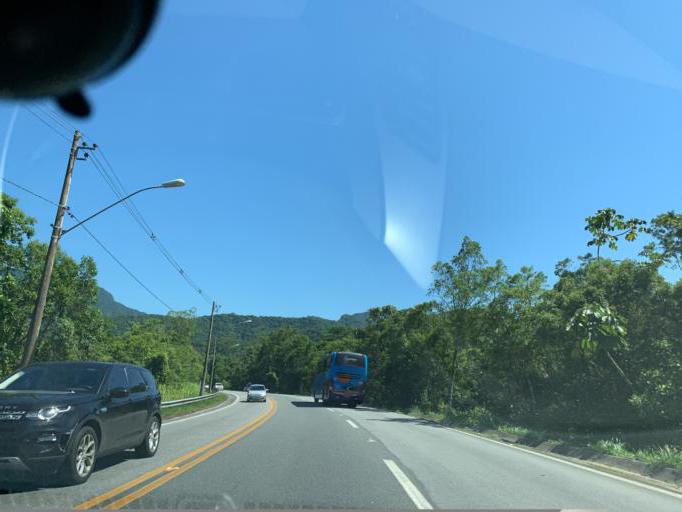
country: BR
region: Sao Paulo
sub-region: Bertioga
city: Bertioga
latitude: -23.7654
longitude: -46.0367
